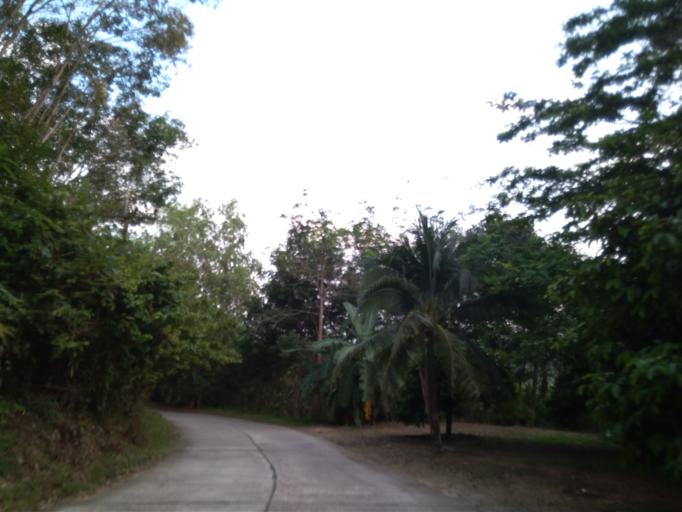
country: TH
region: Phangnga
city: Ko Yao
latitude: 8.1378
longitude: 98.6171
